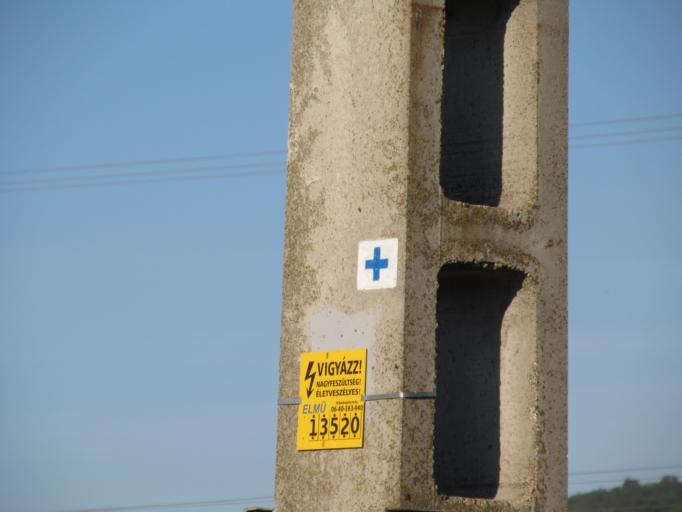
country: HU
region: Komarom-Esztergom
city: Esztergom
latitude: 47.8862
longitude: 18.7808
